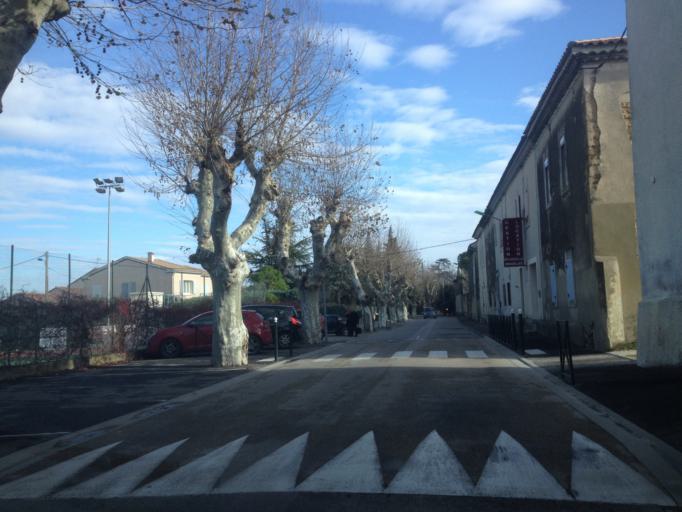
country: FR
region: Provence-Alpes-Cote d'Azur
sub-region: Departement du Vaucluse
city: Bedarrides
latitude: 44.0406
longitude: 4.8909
